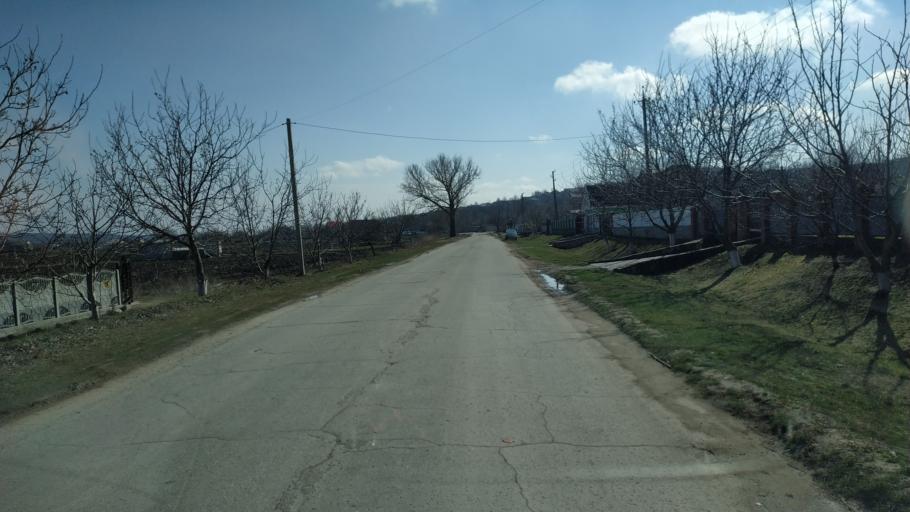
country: MD
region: Hincesti
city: Hincesti
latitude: 46.9373
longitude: 28.6369
